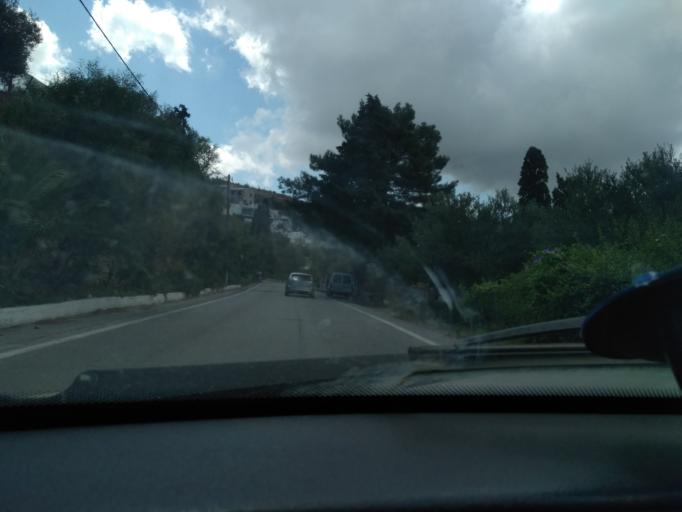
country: GR
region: Crete
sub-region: Nomos Lasithiou
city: Makry-Gialos
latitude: 35.0940
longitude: 26.0710
